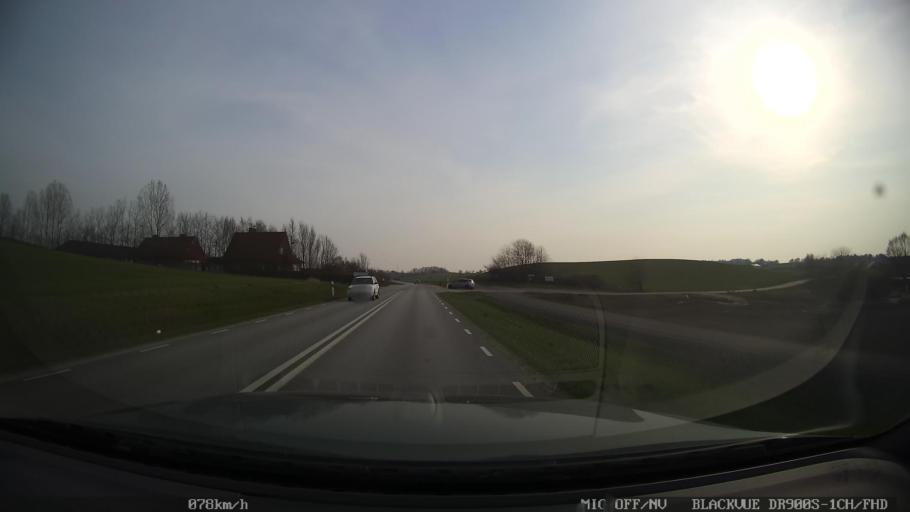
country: SE
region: Skane
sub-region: Ystads Kommun
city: Ystad
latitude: 55.4617
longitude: 13.7989
